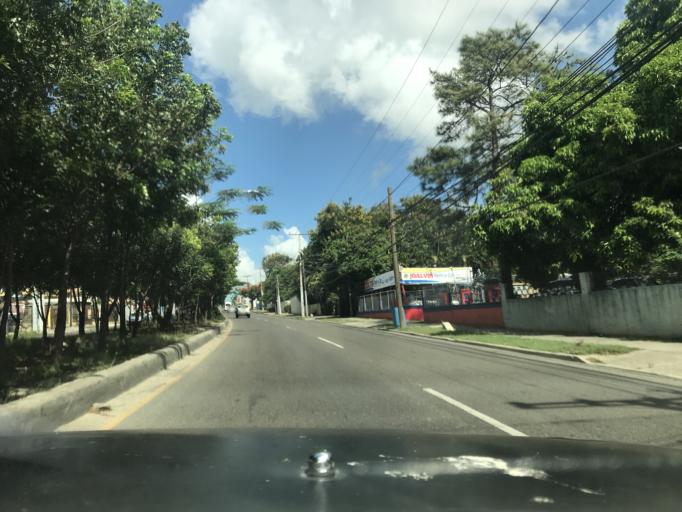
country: DO
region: Santiago
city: Santiago de los Caballeros
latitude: 19.4409
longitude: -70.7279
